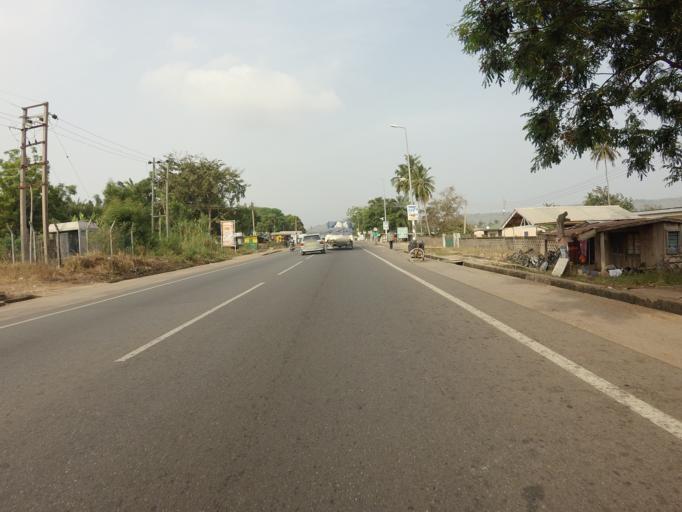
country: GH
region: Volta
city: Ho
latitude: 6.6043
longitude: 0.4785
